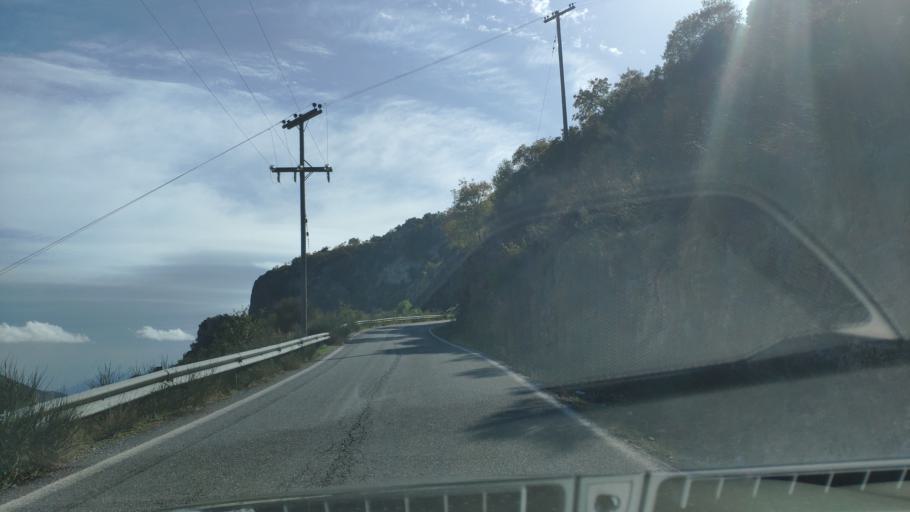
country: GR
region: Peloponnese
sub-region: Nomos Arkadias
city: Dimitsana
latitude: 37.5969
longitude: 22.0307
